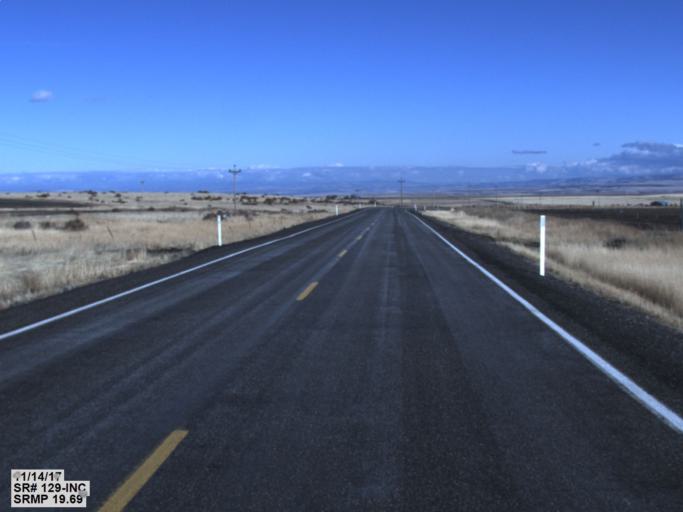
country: US
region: Washington
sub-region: Asotin County
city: Asotin
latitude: 46.1600
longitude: -117.1052
